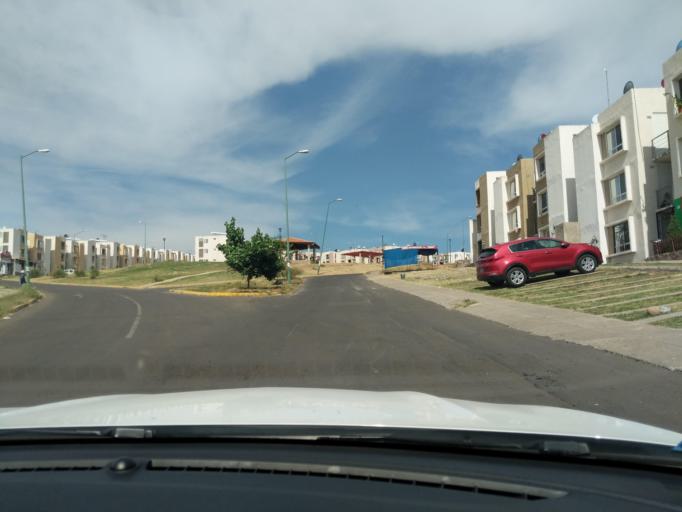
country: MX
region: Jalisco
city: San Jose del Castillo
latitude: 20.5204
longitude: -103.2252
